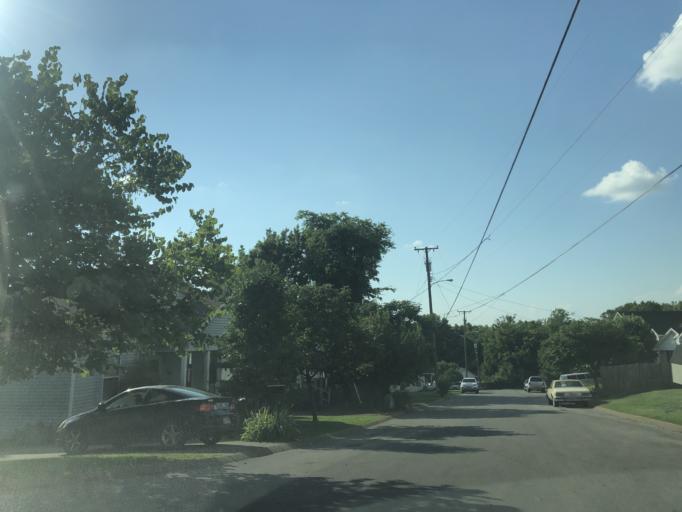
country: US
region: Tennessee
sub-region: Davidson County
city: Nashville
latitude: 36.1592
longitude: -86.8355
